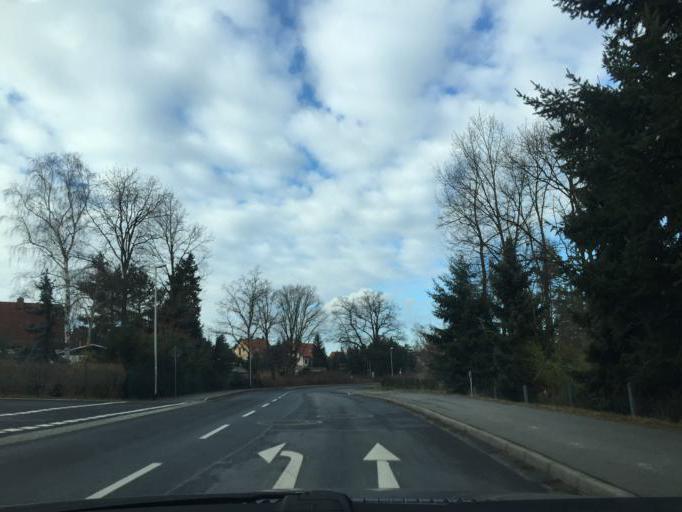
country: DE
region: Saxony
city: Ottendorf-Okrilla
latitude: 51.1846
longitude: 13.7836
